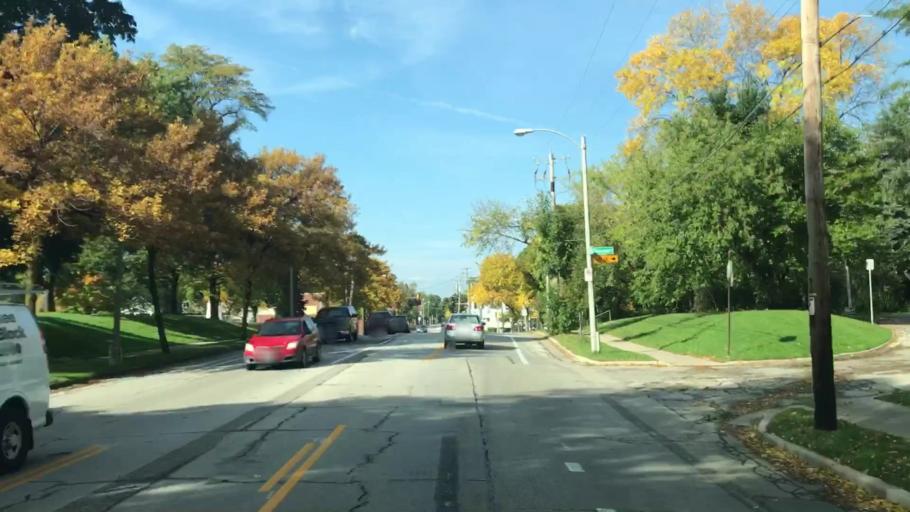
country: US
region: Wisconsin
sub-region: Milwaukee County
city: Shorewood
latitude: 43.0711
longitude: -87.8959
